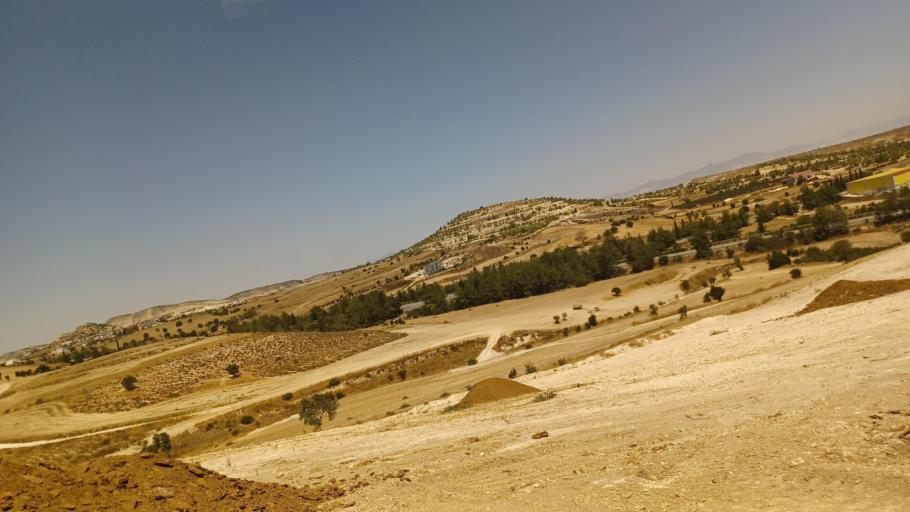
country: CY
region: Lefkosia
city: Lympia
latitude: 34.9910
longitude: 33.4872
